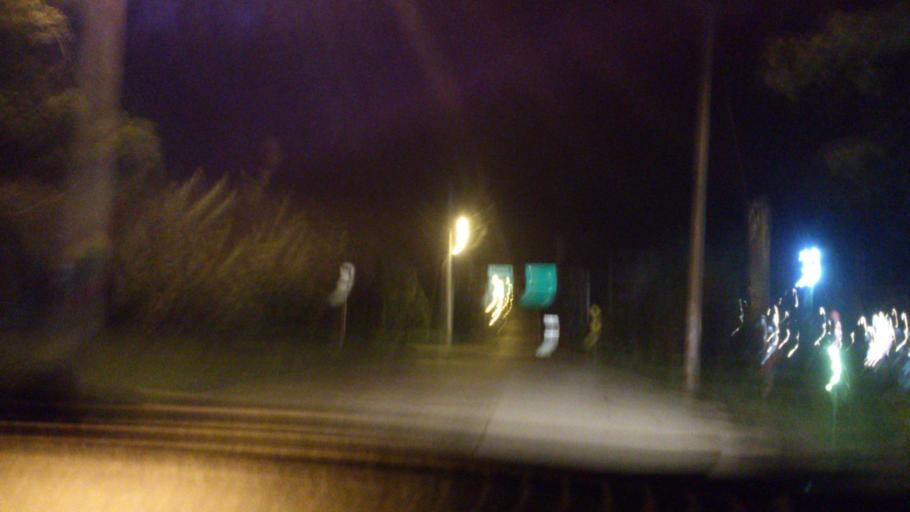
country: CO
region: Valle del Cauca
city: Buga
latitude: 3.8999
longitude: -76.3102
